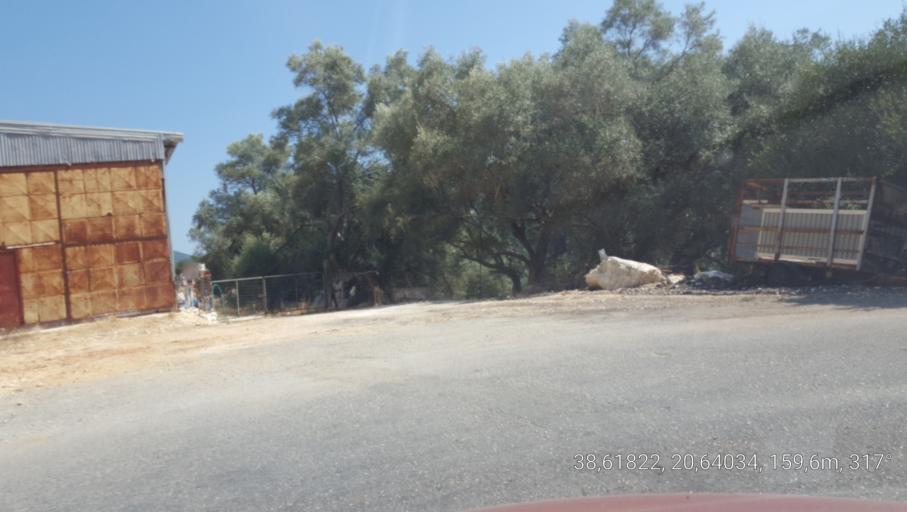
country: GR
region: Ionian Islands
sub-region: Lefkada
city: Nidri
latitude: 38.6181
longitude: 20.6403
